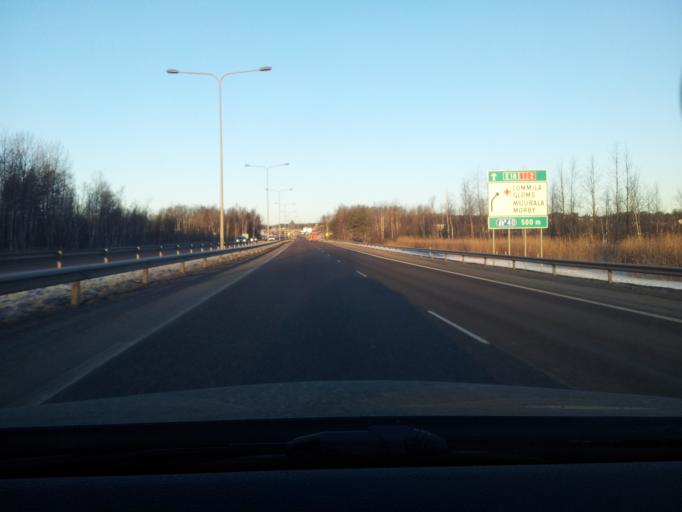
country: FI
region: Uusimaa
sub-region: Helsinki
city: Espoo
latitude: 60.2122
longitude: 24.6738
